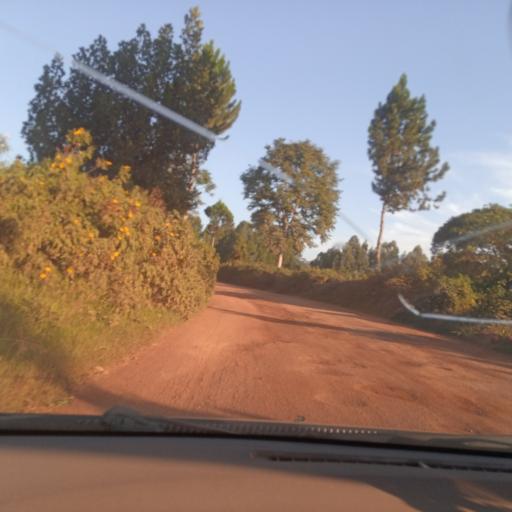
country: UG
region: Central Region
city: Masaka
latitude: -0.3327
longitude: 31.7582
